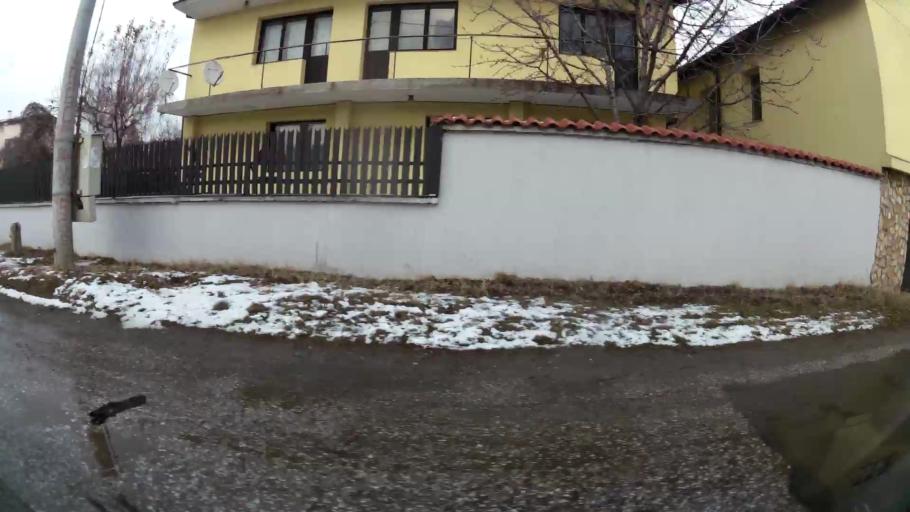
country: BG
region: Sofia-Capital
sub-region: Stolichna Obshtina
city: Sofia
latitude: 42.6967
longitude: 23.3677
